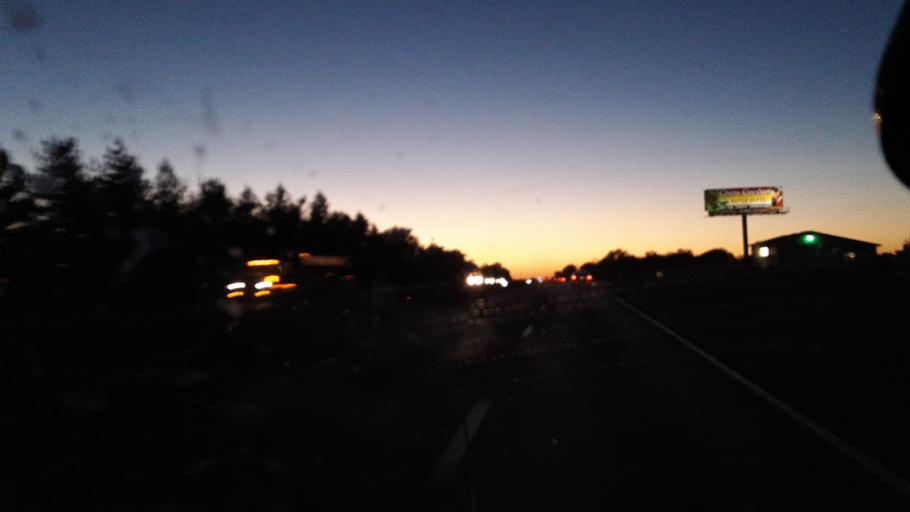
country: US
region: Missouri
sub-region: Boone County
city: Hallsville
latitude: 38.9538
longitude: -92.1149
